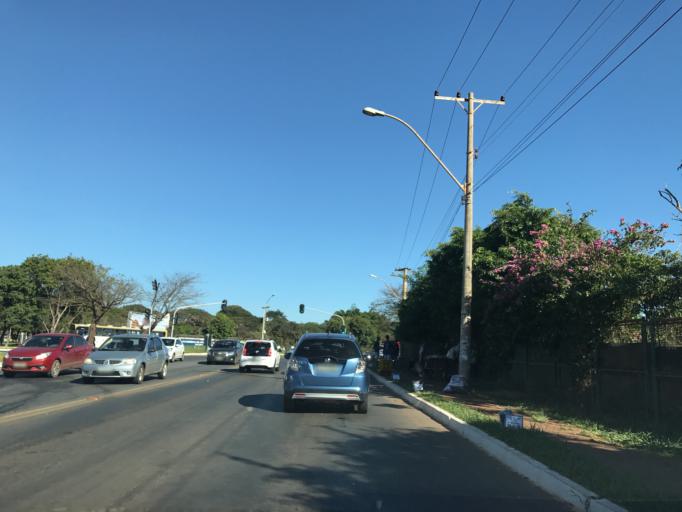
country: BR
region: Federal District
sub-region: Brasilia
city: Brasilia
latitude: -15.8248
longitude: -47.9331
